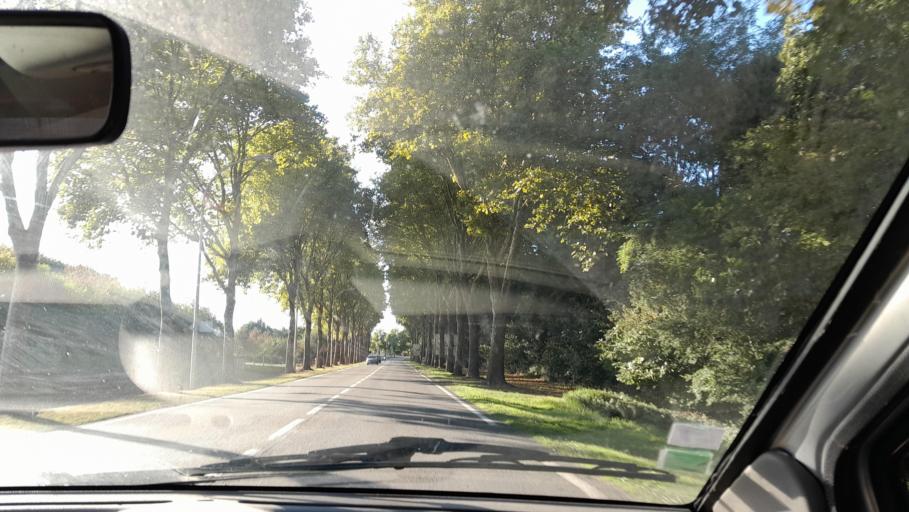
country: FR
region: Pays de la Loire
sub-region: Departement de la Mayenne
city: Craon
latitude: 47.8443
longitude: -0.9606
